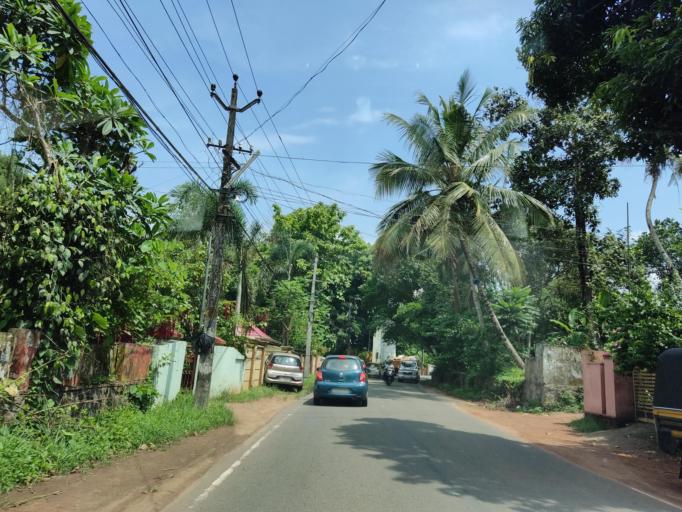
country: IN
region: Kerala
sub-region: Alappuzha
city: Chengannur
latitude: 9.3051
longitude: 76.5885
